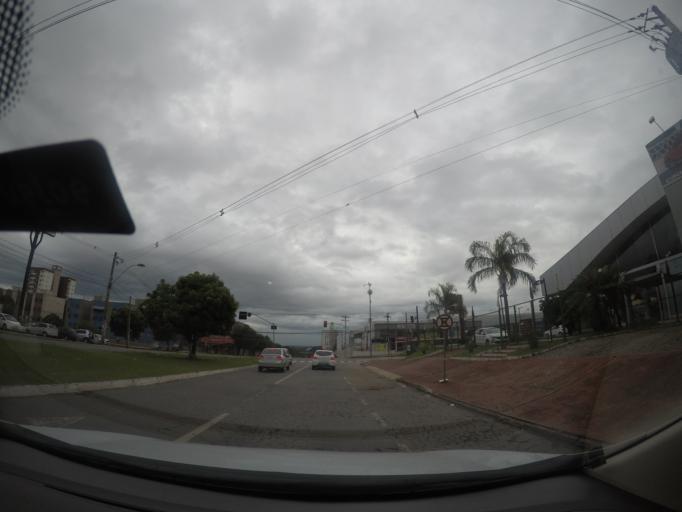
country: BR
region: Goias
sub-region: Goiania
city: Goiania
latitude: -16.7393
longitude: -49.2727
